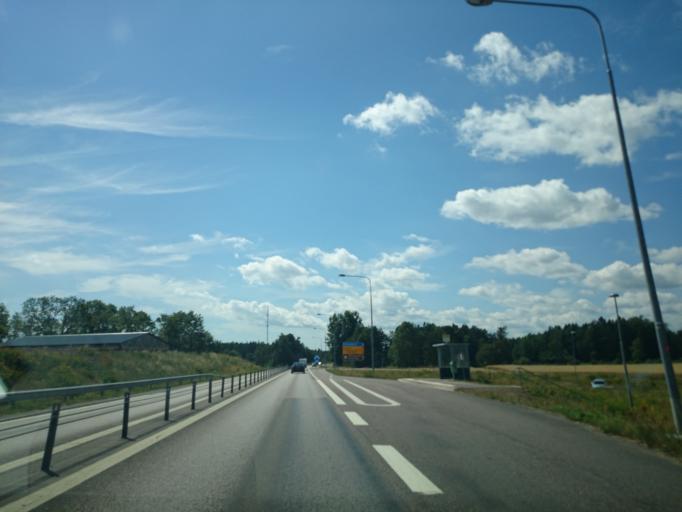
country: SE
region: Kalmar
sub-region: Monsteras Kommun
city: Timmernabben
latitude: 56.8499
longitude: 16.3774
